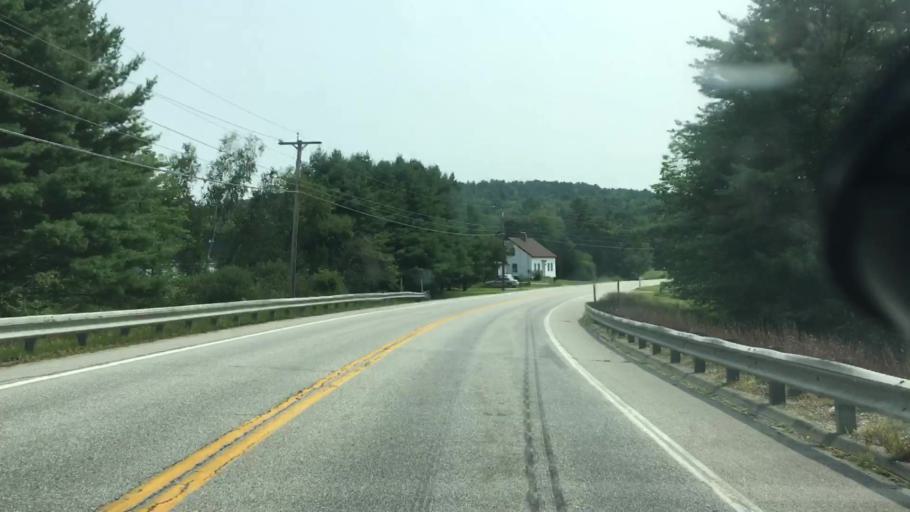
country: US
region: Maine
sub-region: Androscoggin County
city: Livermore Falls
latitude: 44.4463
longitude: -70.1536
